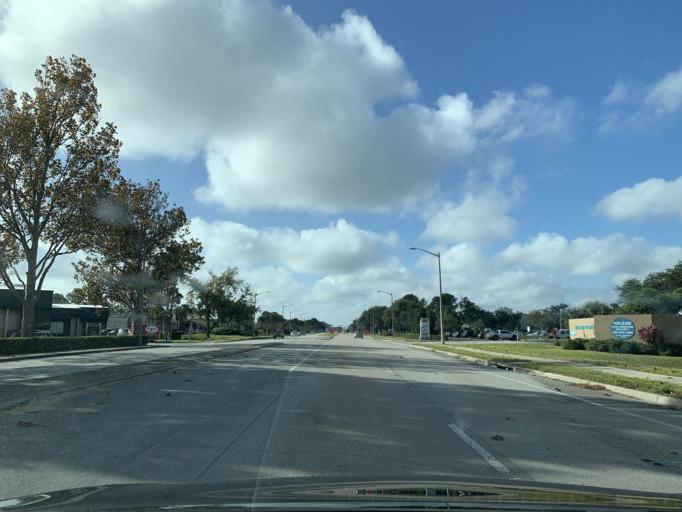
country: US
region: Florida
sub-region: Orange County
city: Oak Ridge
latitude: 28.5028
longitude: -81.4296
